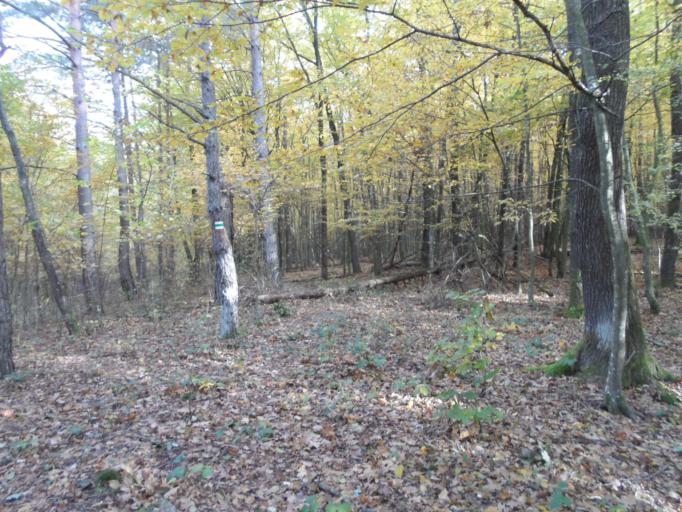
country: SI
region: Hodos-Hodos
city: Hodos
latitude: 46.8297
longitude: 16.3512
